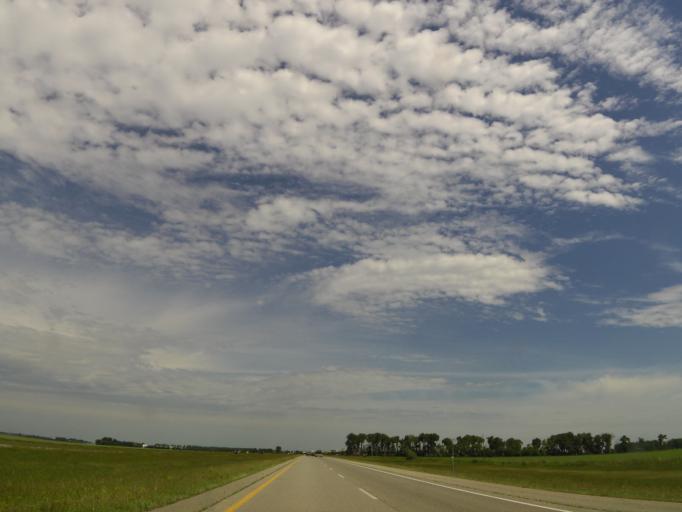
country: US
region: North Dakota
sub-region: Grand Forks County
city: Grand Forks
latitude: 47.8188
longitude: -97.0776
